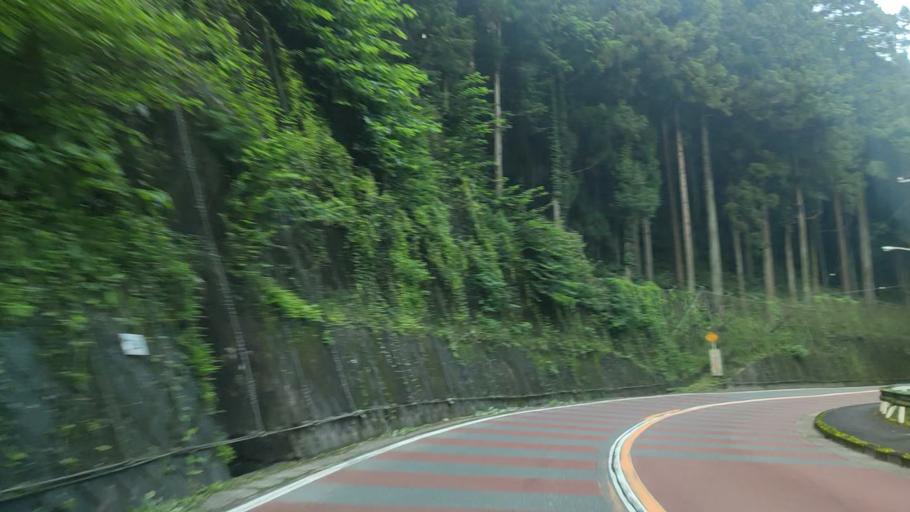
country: JP
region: Tokyo
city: Ome
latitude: 35.8374
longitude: 139.2116
